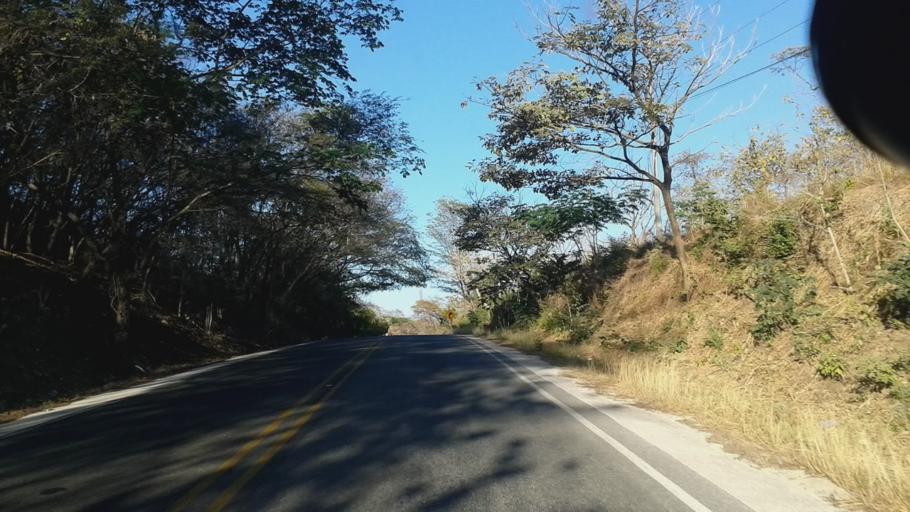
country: CR
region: Guanacaste
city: Nandayure
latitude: 10.2219
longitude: -85.1955
